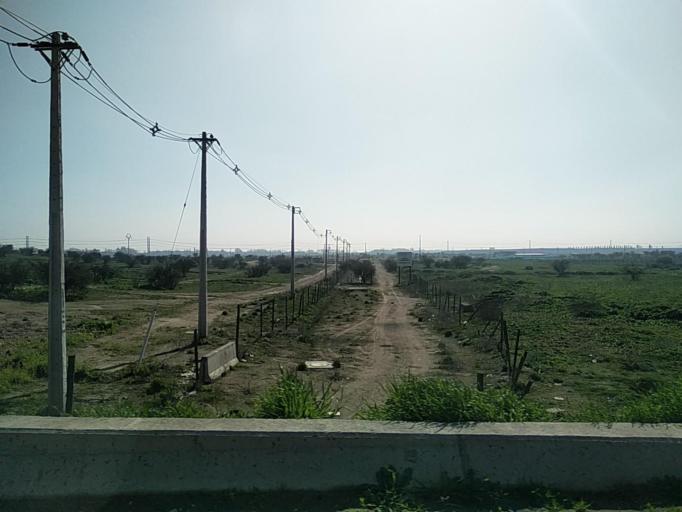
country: CL
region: Santiago Metropolitan
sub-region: Provincia de Santiago
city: Lo Prado
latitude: -33.4403
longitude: -70.8063
